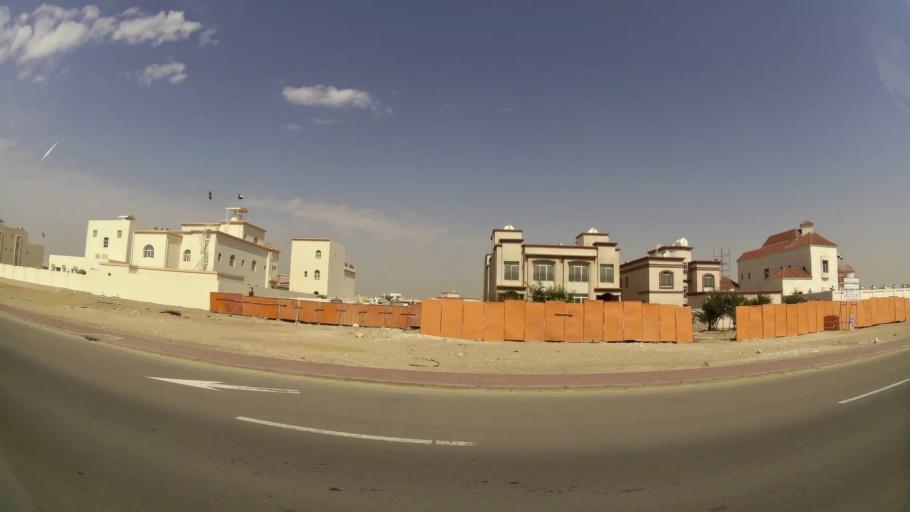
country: AE
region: Abu Dhabi
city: Abu Dhabi
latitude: 24.3121
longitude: 54.5442
